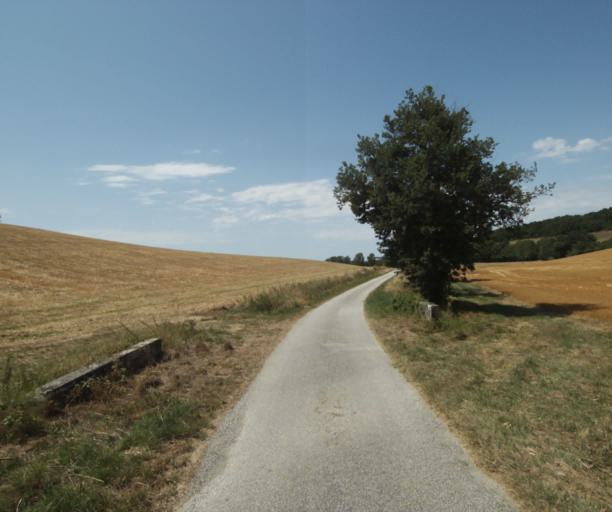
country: FR
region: Midi-Pyrenees
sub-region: Departement de la Haute-Garonne
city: Saint-Felix-Lauragais
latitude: 43.4620
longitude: 1.8577
